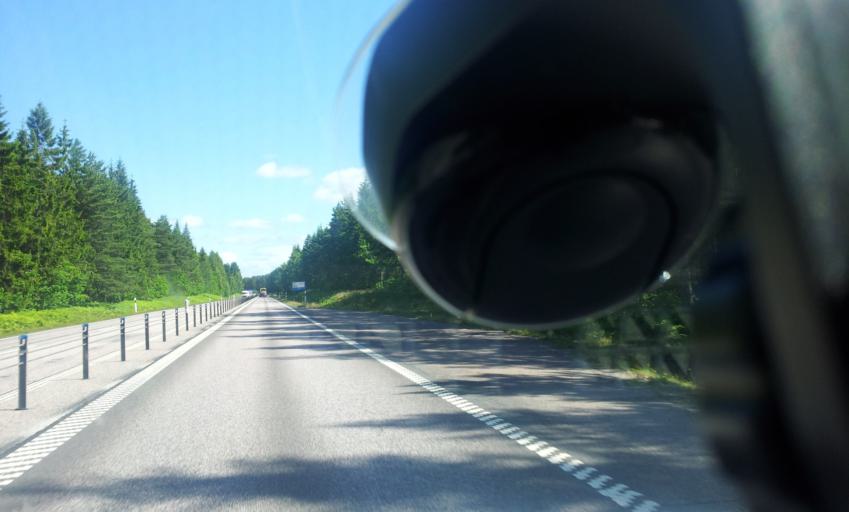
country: SE
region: Kalmar
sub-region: Monsteras Kommun
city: Moensteras
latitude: 57.0126
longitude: 16.4244
